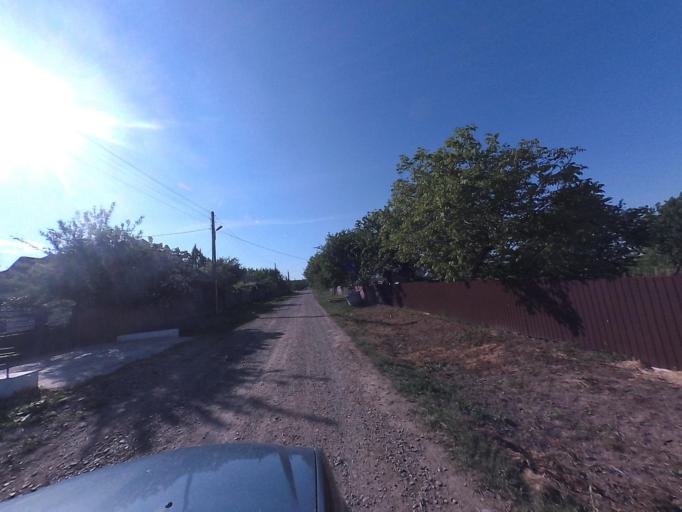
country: RO
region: Neamt
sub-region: Comuna Dulcesti
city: Dulcesti
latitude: 47.0038
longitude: 26.7729
